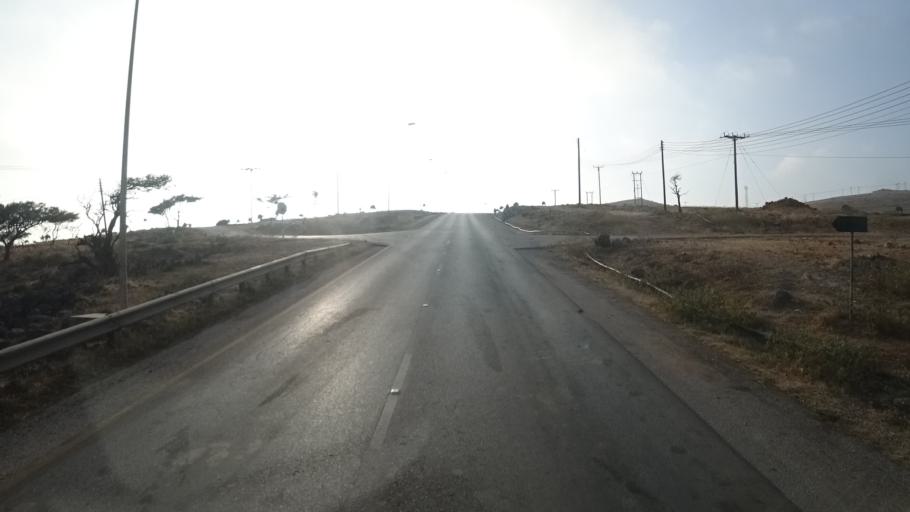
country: OM
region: Zufar
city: Salalah
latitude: 17.1198
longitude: 53.9816
